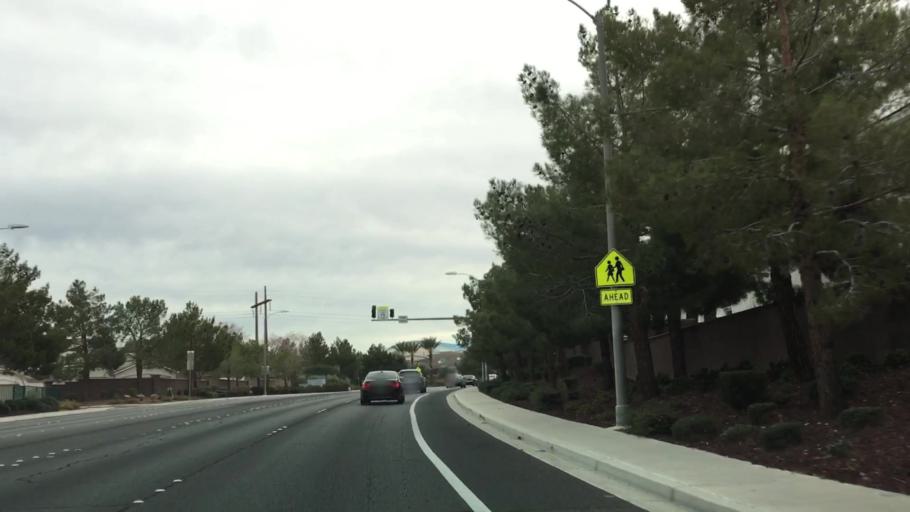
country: US
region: Nevada
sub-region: Clark County
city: Whitney
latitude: 36.0170
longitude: -115.0916
